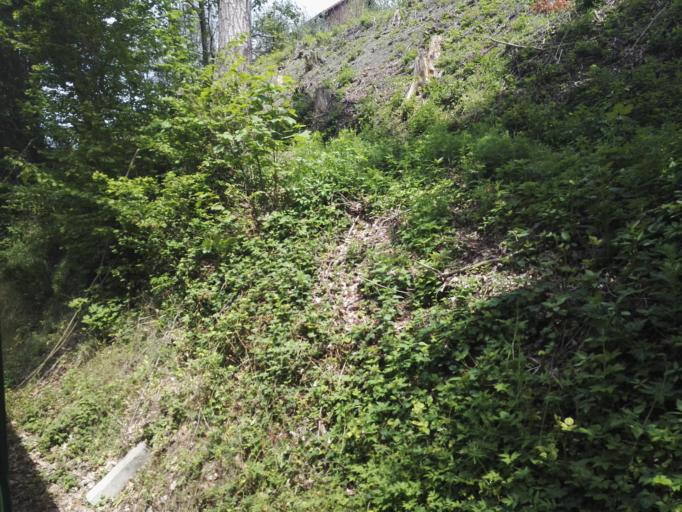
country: AT
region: Styria
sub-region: Politischer Bezirk Weiz
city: Anger
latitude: 47.2852
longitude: 15.6911
